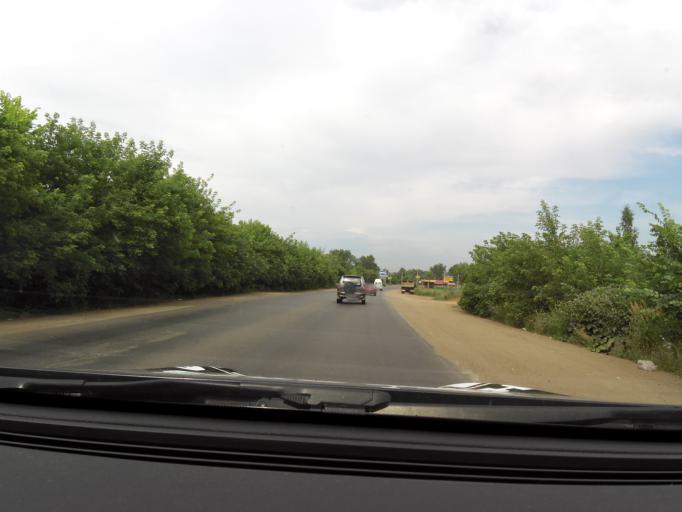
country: RU
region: Bashkortostan
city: Iglino
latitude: 54.7768
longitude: 56.2337
